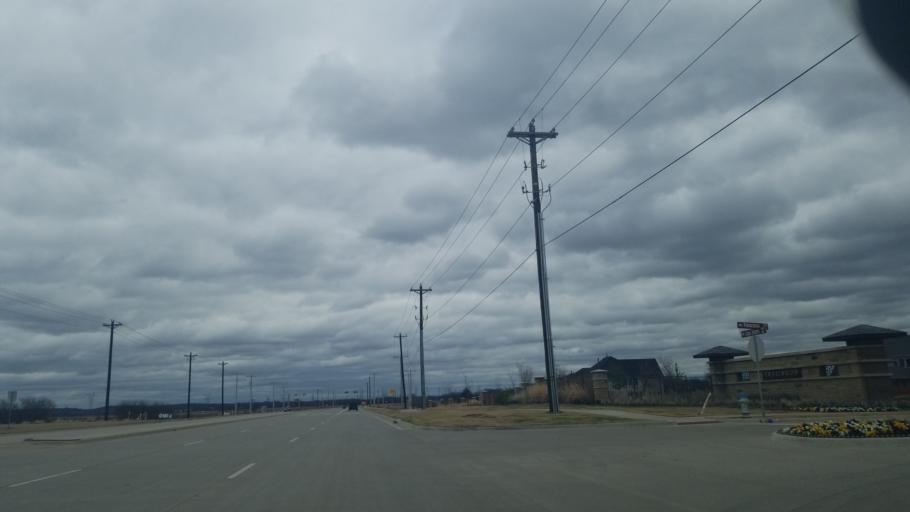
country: US
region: Texas
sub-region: Denton County
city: Roanoke
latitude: 33.0587
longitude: -97.2120
